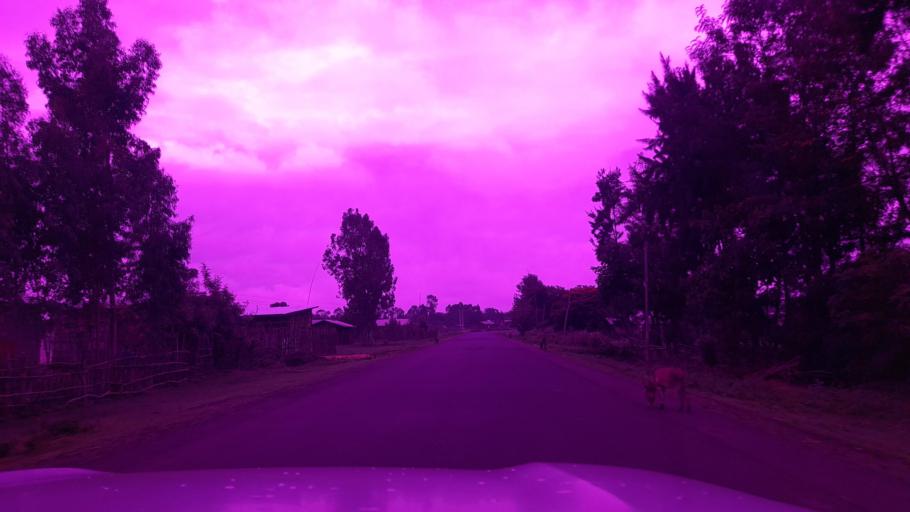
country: ET
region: Oromiya
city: Waliso
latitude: 8.2715
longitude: 37.6611
